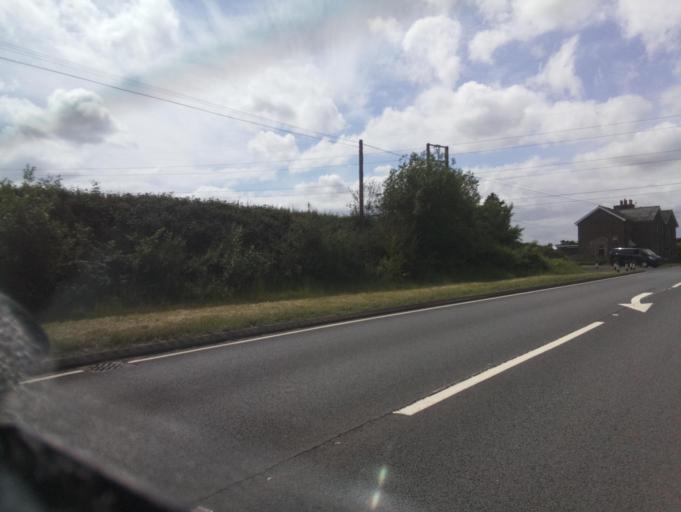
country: GB
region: England
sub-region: Herefordshire
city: Sellack
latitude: 51.9231
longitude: -2.6565
